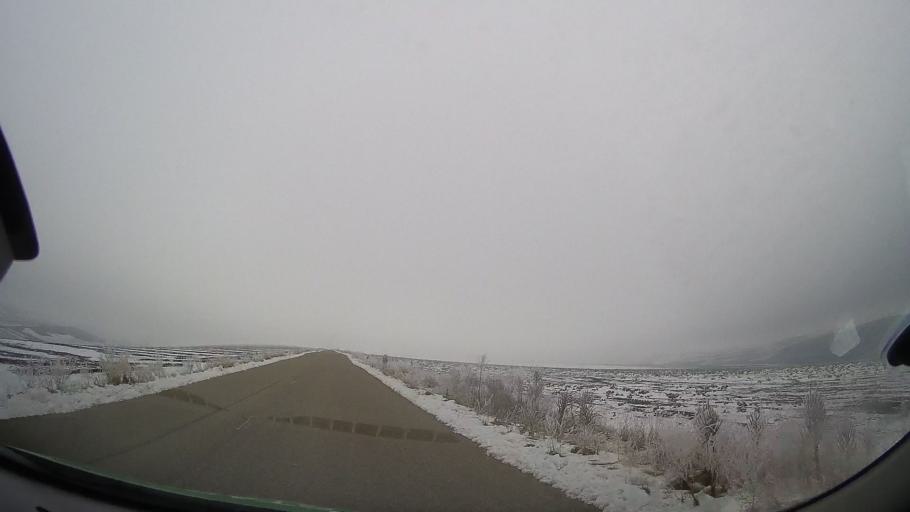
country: RO
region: Vaslui
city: Coroiesti
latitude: 46.2125
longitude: 27.4816
